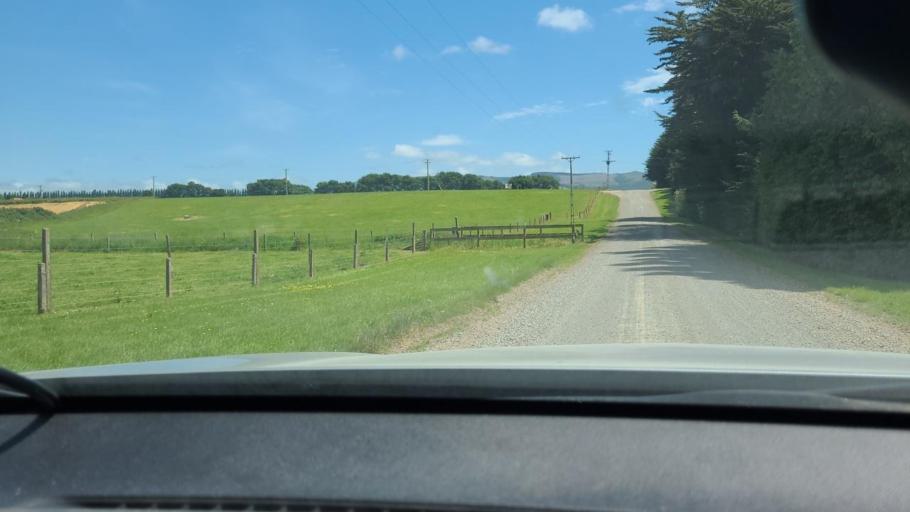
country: NZ
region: Southland
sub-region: Southland District
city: Riverton
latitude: -46.0420
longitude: 168.0145
